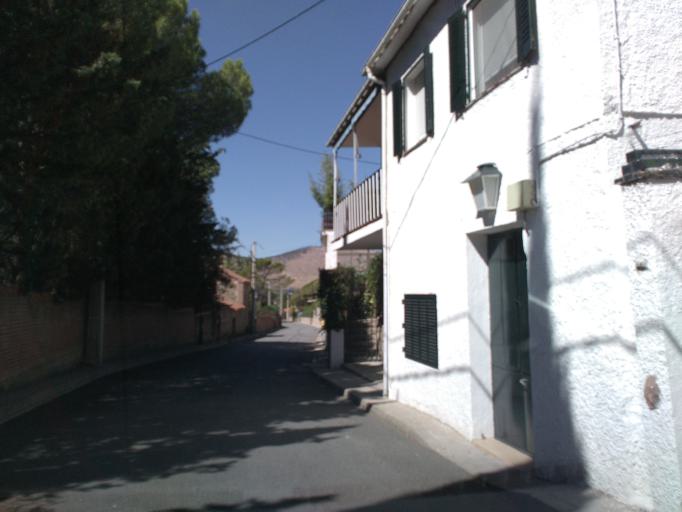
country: ES
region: Madrid
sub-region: Provincia de Madrid
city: Robledo de Chavela
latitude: 40.5196
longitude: -4.2469
